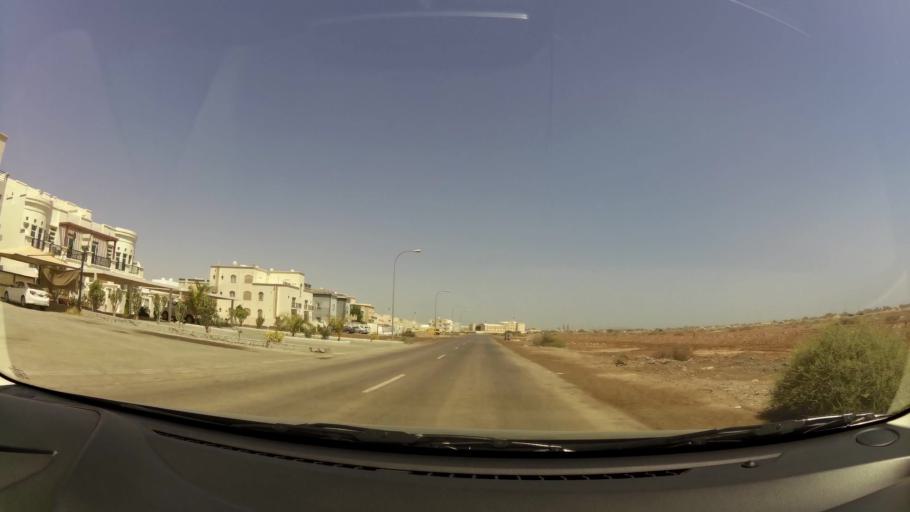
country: OM
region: Muhafazat Masqat
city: As Sib al Jadidah
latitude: 23.6262
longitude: 58.2562
